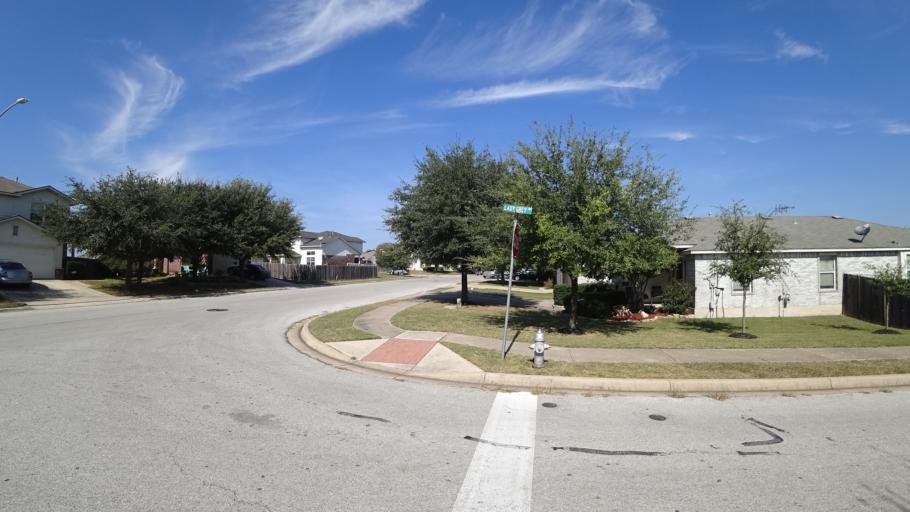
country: US
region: Texas
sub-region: Travis County
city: Pflugerville
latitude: 30.4235
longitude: -97.6377
